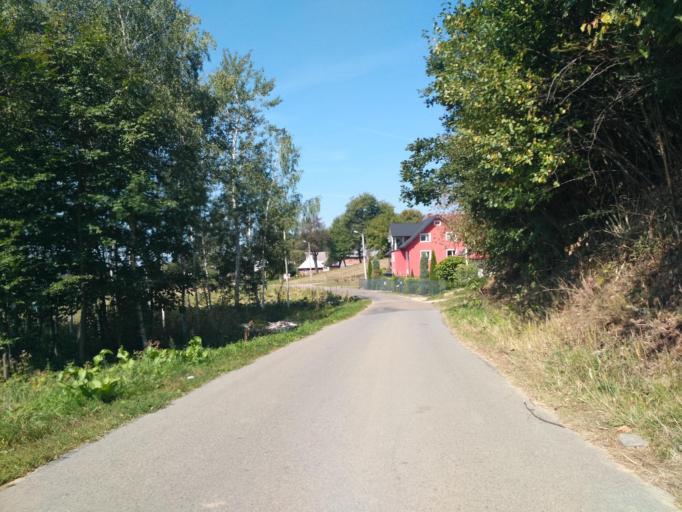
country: PL
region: Subcarpathian Voivodeship
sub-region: Powiat brzozowski
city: Grabownica Starzenska
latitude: 49.6458
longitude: 22.0983
